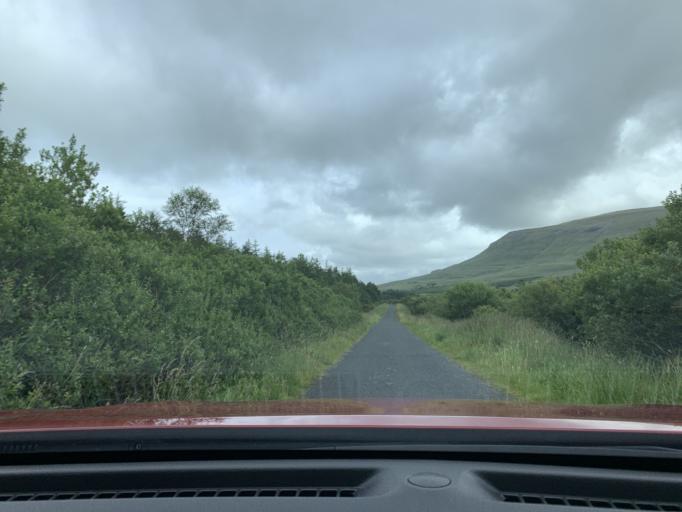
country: IE
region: Connaught
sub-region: Sligo
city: Sligo
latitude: 54.3837
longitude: -8.4104
